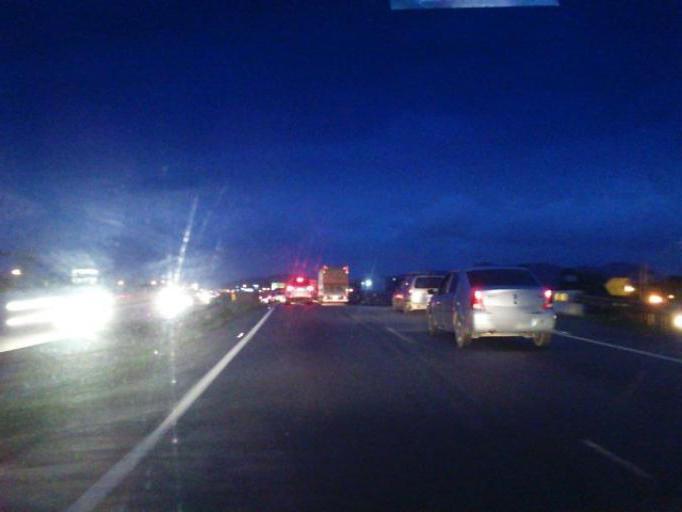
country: BR
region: Santa Catarina
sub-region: Itajai
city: Itajai
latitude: -26.8694
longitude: -48.7299
